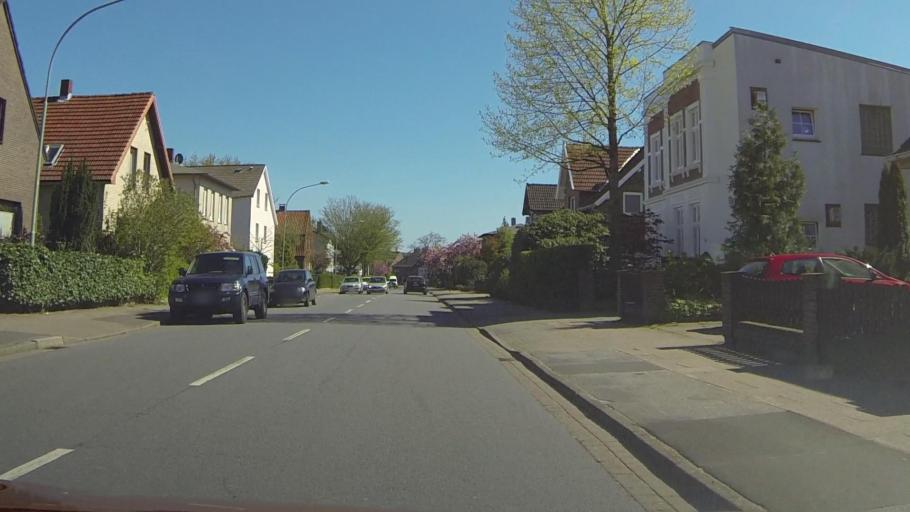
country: DE
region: Schleswig-Holstein
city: Pinneberg
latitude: 53.6668
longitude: 9.7875
